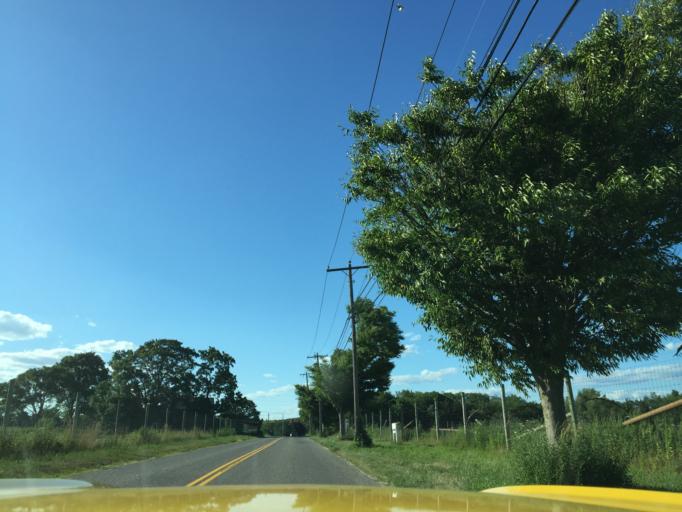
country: US
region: New York
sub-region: Suffolk County
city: Southold
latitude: 41.0676
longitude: -72.4350
